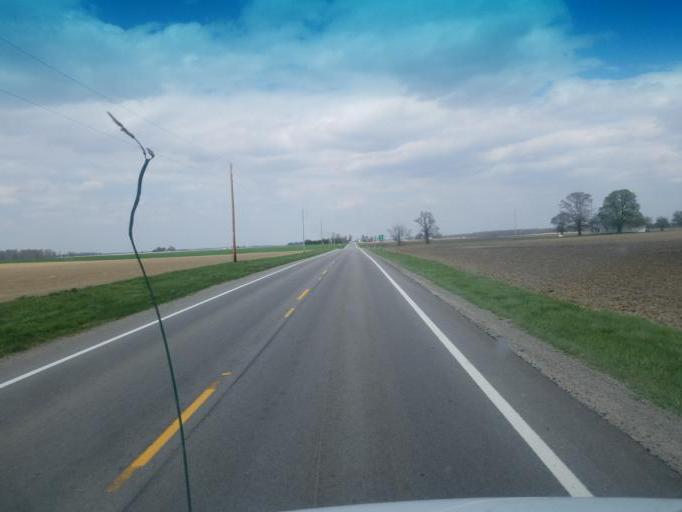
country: US
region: Ohio
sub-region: Wyandot County
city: Upper Sandusky
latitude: 40.8892
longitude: -83.2764
